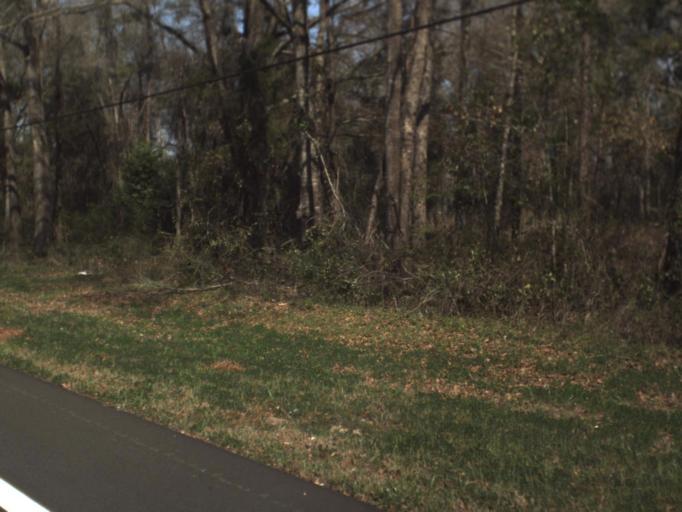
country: US
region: Florida
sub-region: Jackson County
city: Sneads
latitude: 30.8210
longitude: -85.0479
